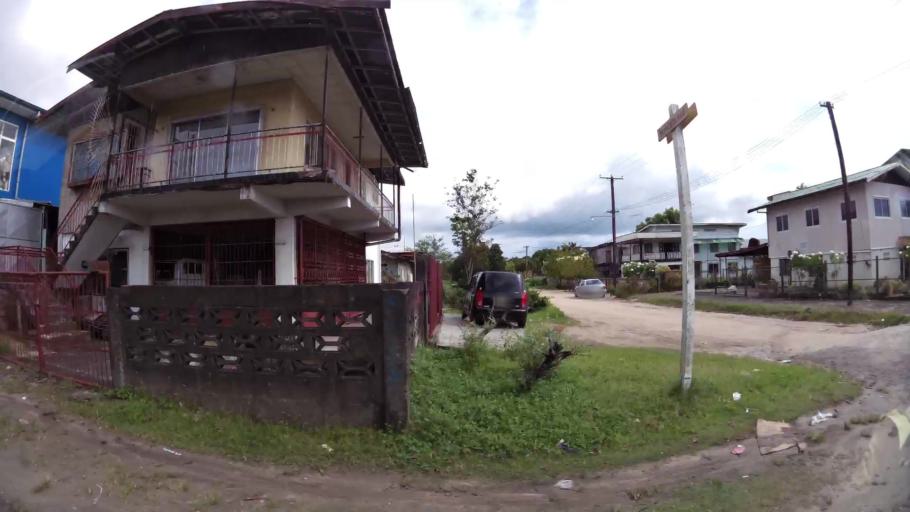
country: SR
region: Paramaribo
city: Paramaribo
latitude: 5.8419
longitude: -55.1951
